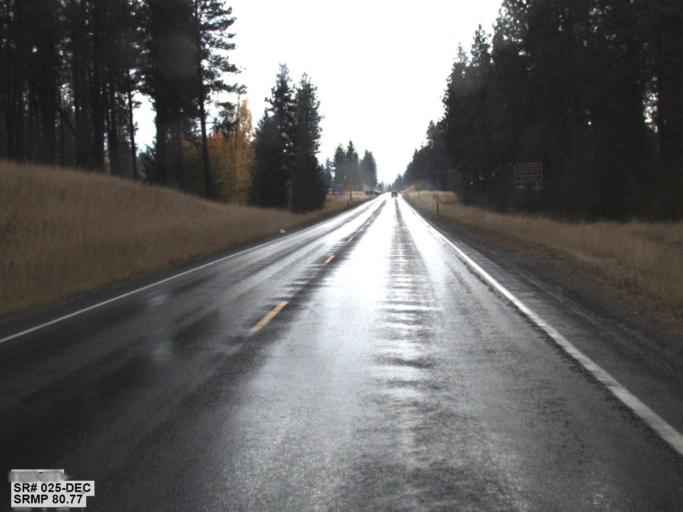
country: US
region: Washington
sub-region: Stevens County
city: Kettle Falls
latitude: 48.6019
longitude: -118.0752
